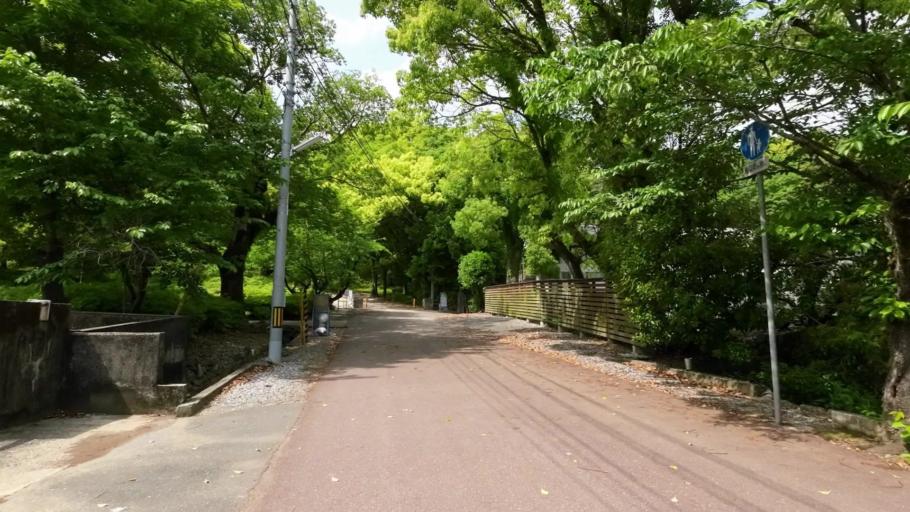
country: JP
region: Kochi
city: Kochi-shi
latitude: 33.5595
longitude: 133.5299
